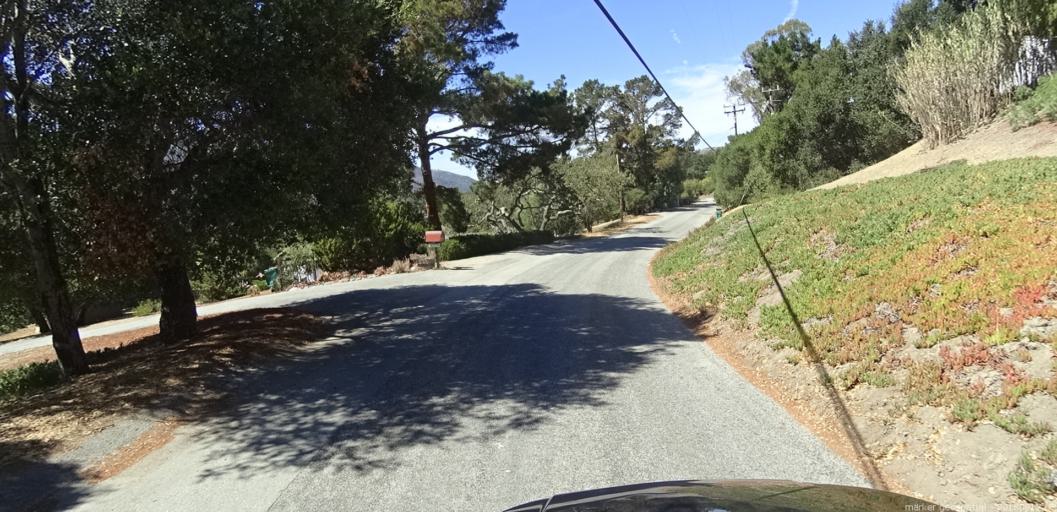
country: US
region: California
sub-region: Monterey County
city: Carmel Valley Village
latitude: 36.4946
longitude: -121.7423
